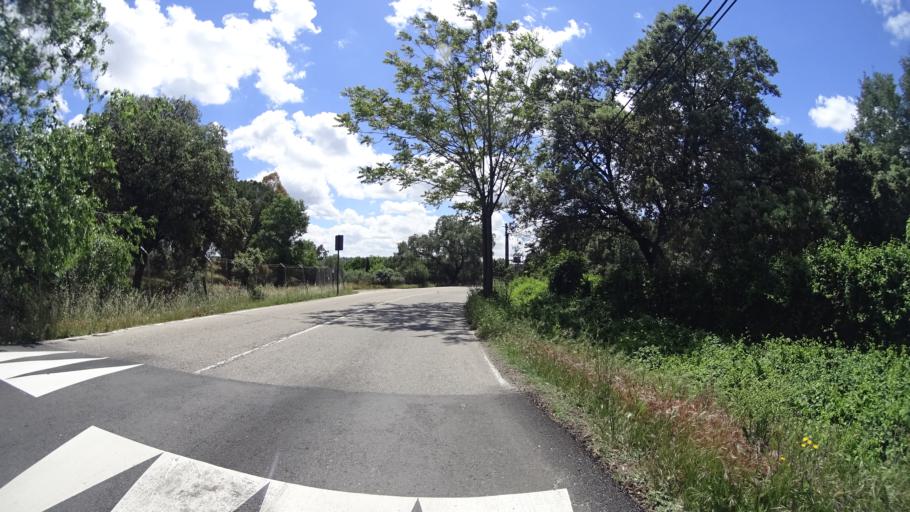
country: ES
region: Madrid
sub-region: Provincia de Madrid
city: Villanueva del Pardillo
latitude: 40.4623
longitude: -3.9457
